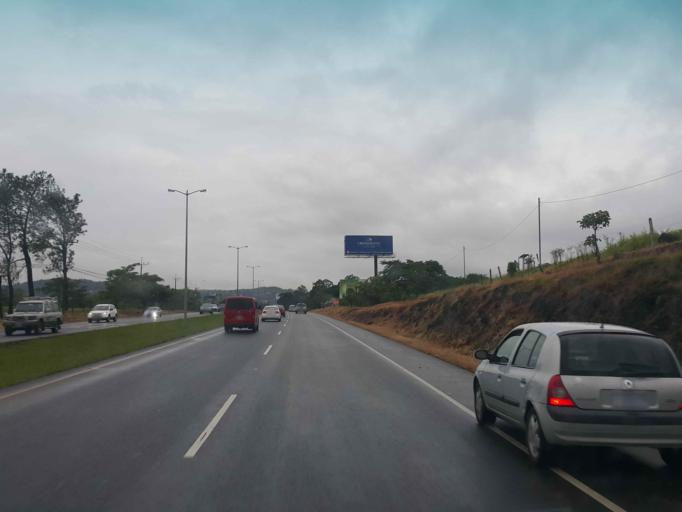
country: CR
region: San Jose
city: Santa Ana
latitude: 9.9374
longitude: -84.2106
